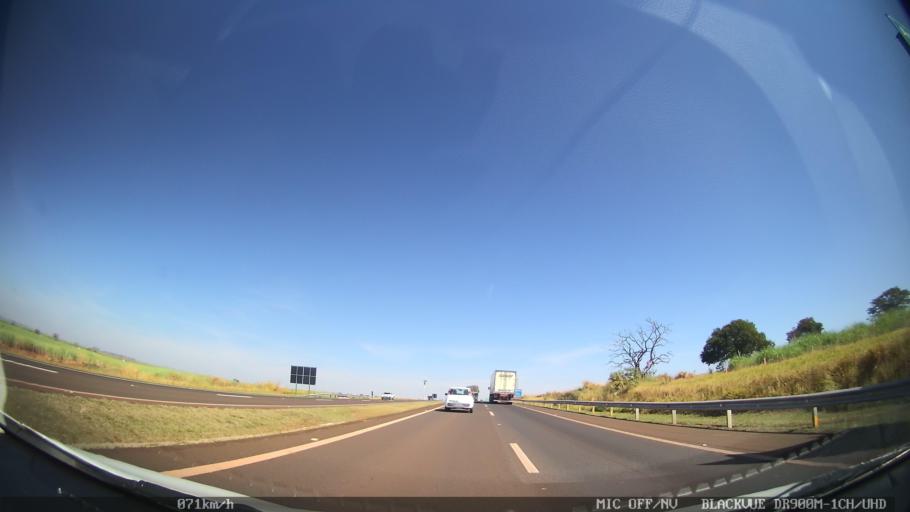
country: BR
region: Sao Paulo
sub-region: Ribeirao Preto
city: Ribeirao Preto
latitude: -21.1597
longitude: -47.8959
